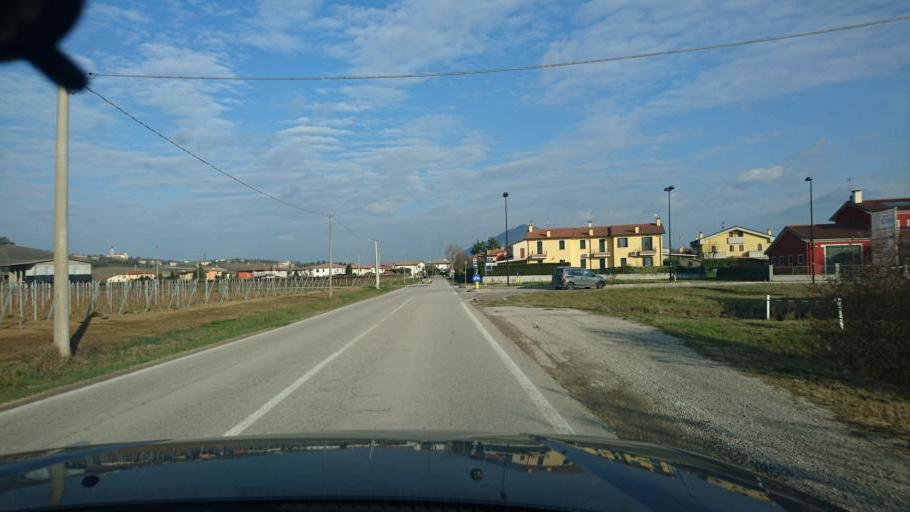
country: IT
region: Veneto
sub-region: Provincia di Vicenza
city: Albettone
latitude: 45.3580
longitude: 11.5761
